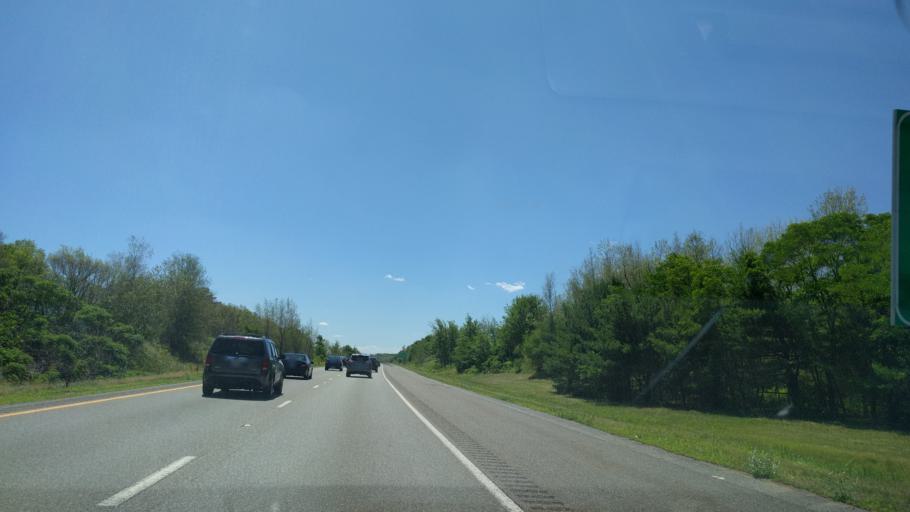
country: US
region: Massachusetts
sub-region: Worcester County
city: Whitinsville
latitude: 42.1128
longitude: -71.7055
